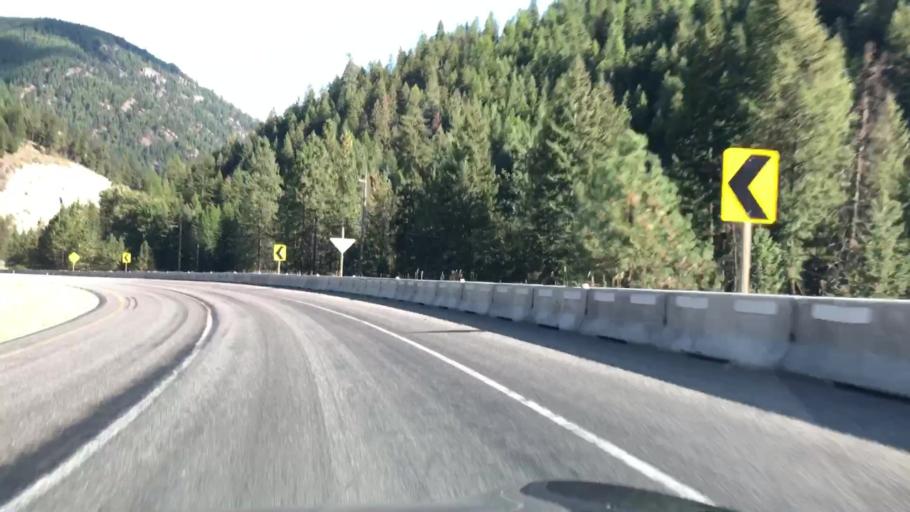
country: US
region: Montana
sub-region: Sanders County
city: Thompson Falls
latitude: 47.3318
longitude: -115.2650
